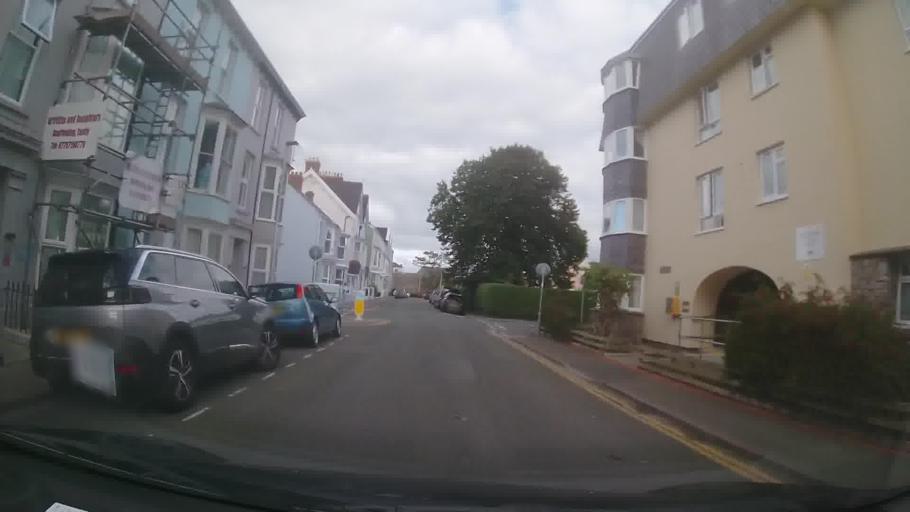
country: GB
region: Wales
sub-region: Pembrokeshire
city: Tenby
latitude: 51.6699
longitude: -4.7019
